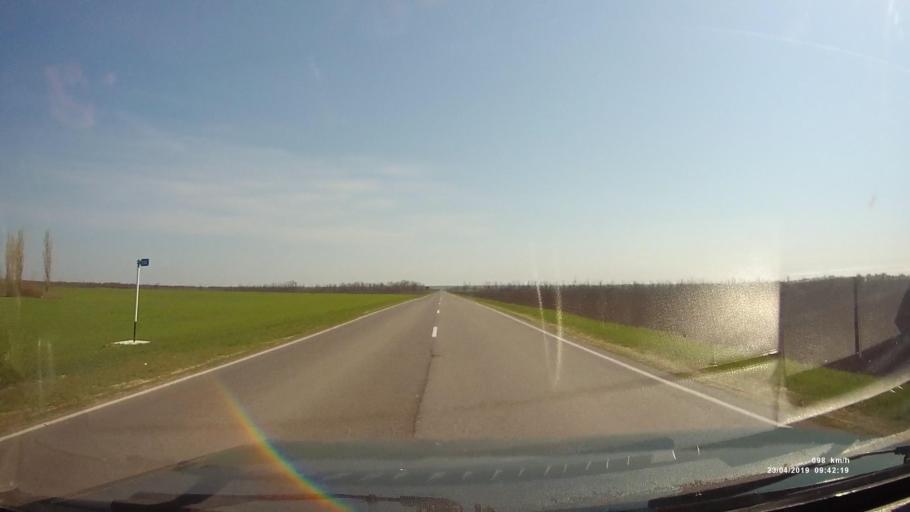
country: RU
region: Rostov
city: Orlovskiy
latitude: 46.8687
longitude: 41.9747
